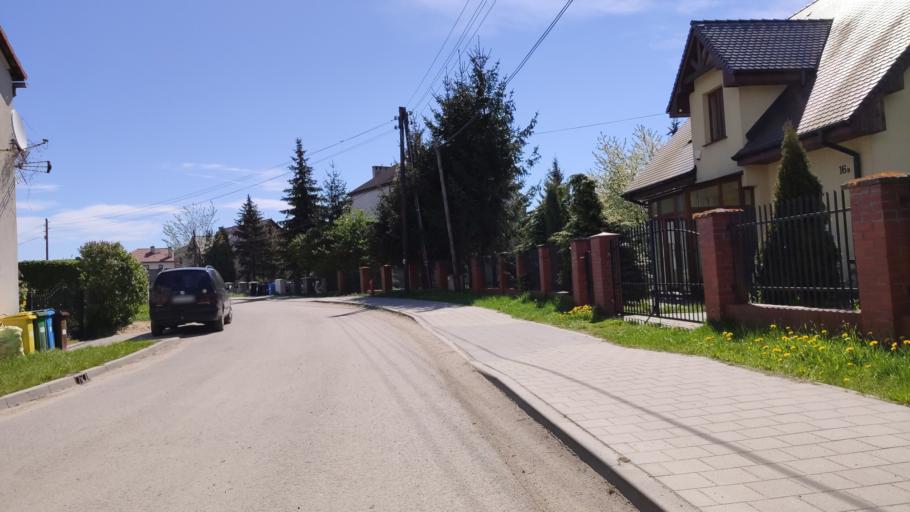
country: PL
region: Lower Silesian Voivodeship
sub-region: Powiat wroclawski
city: Zerniki Wroclawskie
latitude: 51.0482
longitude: 17.0538
